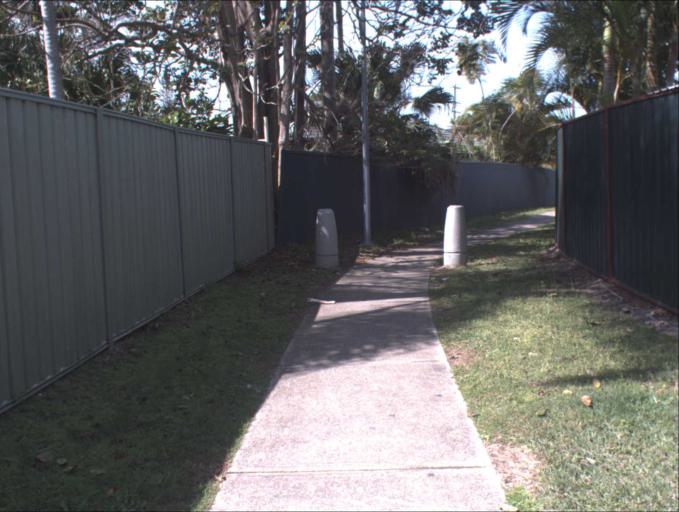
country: AU
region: Queensland
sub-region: Logan
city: Logan Reserve
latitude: -27.6854
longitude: 153.0873
